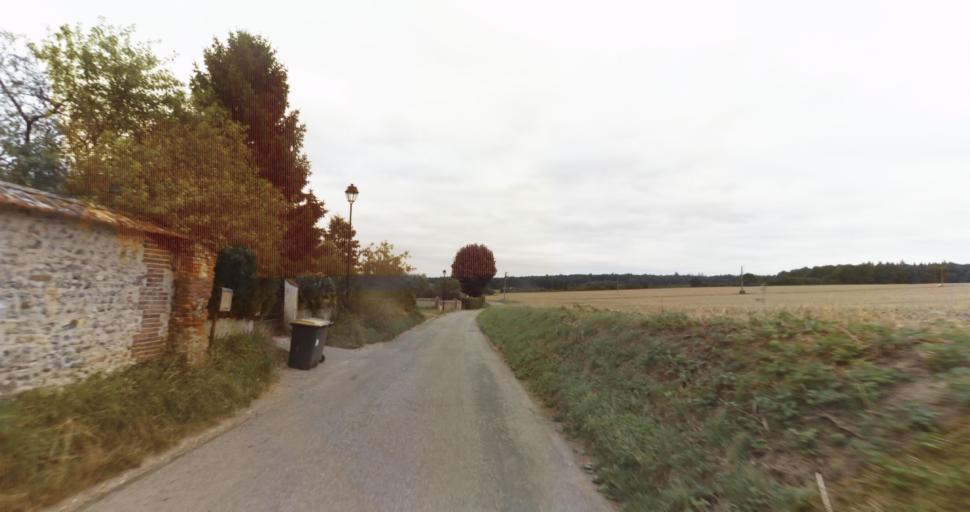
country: FR
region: Haute-Normandie
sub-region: Departement de l'Eure
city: Marcilly-sur-Eure
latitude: 48.8841
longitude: 1.3082
